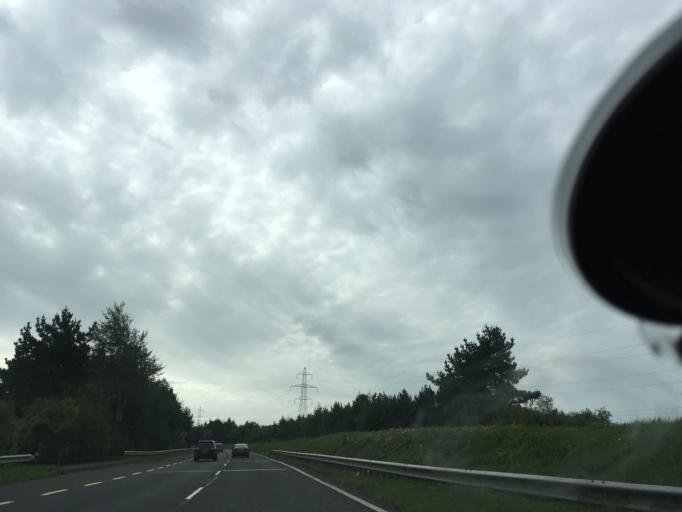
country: IE
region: Leinster
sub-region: Wicklow
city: Kilpedder
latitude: 53.1009
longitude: -6.1074
